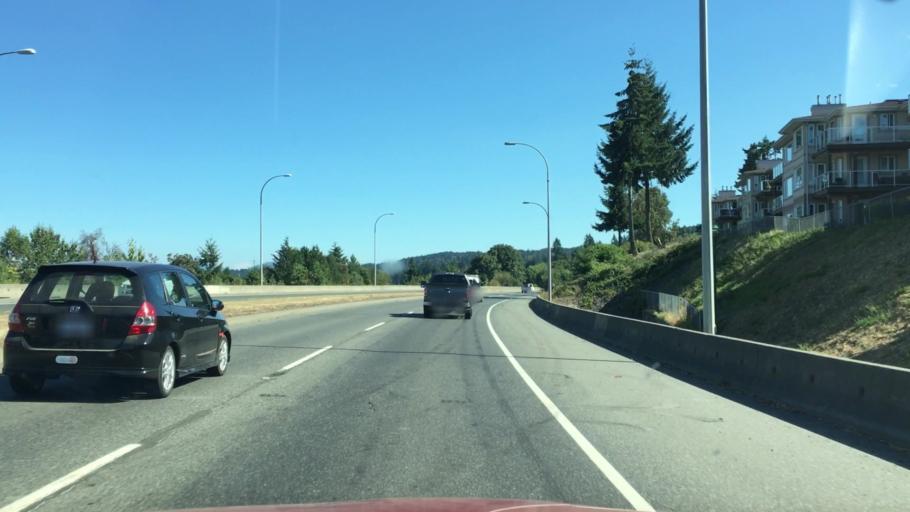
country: CA
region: British Columbia
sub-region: Cowichan Valley Regional District
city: Ladysmith
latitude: 48.9906
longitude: -123.8111
